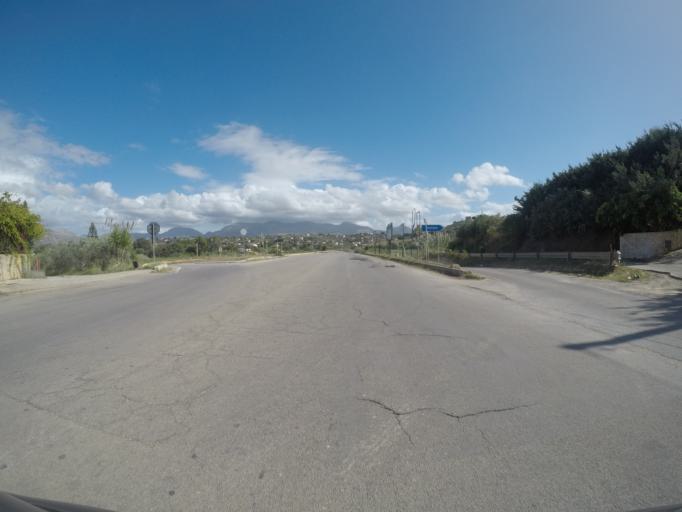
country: IT
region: Sicily
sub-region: Palermo
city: Trappeto
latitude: 38.0701
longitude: 13.0515
